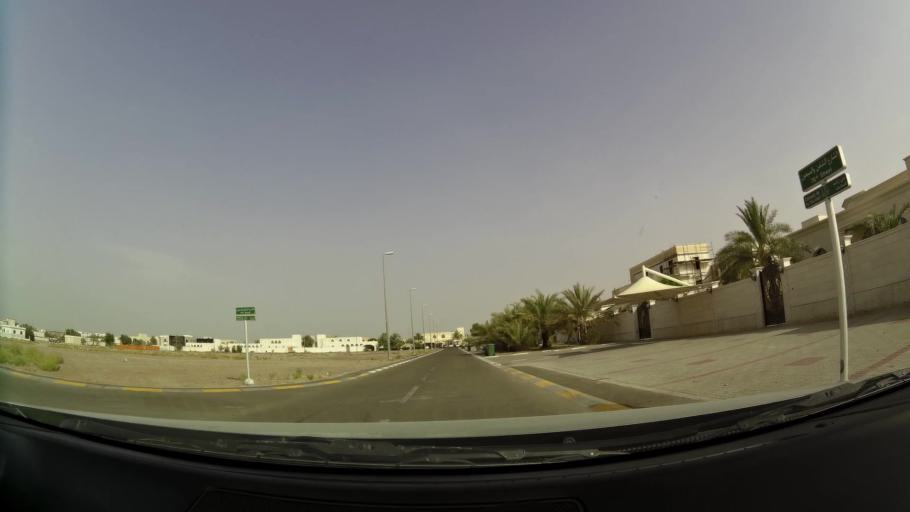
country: AE
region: Abu Dhabi
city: Al Ain
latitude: 24.2074
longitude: 55.5915
